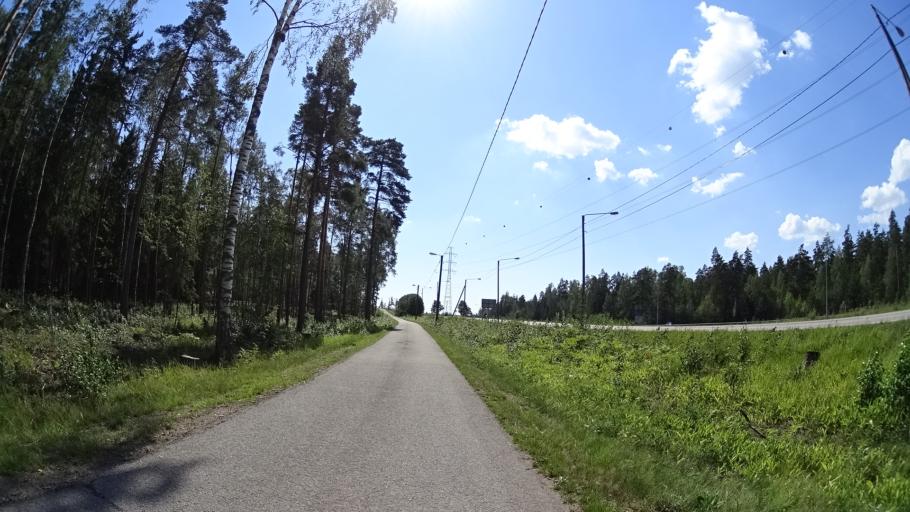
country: FI
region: Uusimaa
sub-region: Helsinki
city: Vantaa
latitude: 60.3144
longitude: 24.9991
